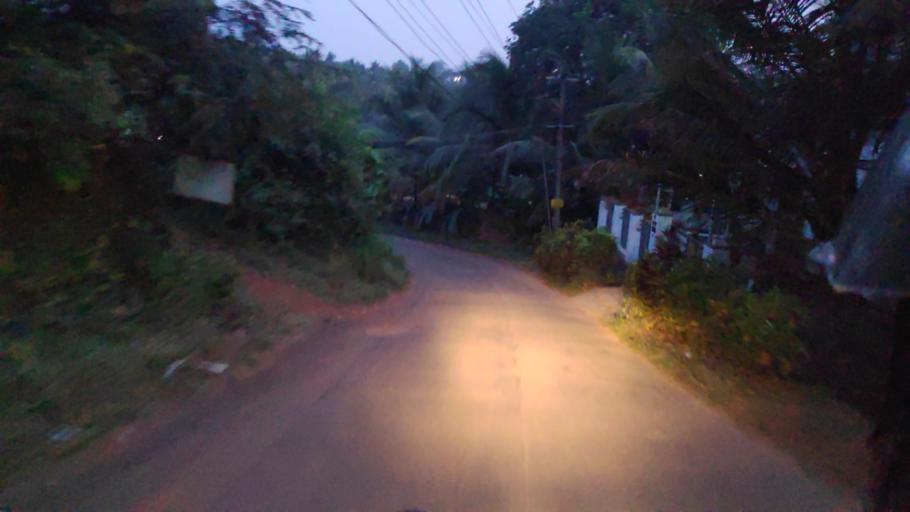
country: IN
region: Kerala
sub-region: Kozhikode
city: Kunnamangalam
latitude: 11.2801
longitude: 75.8331
